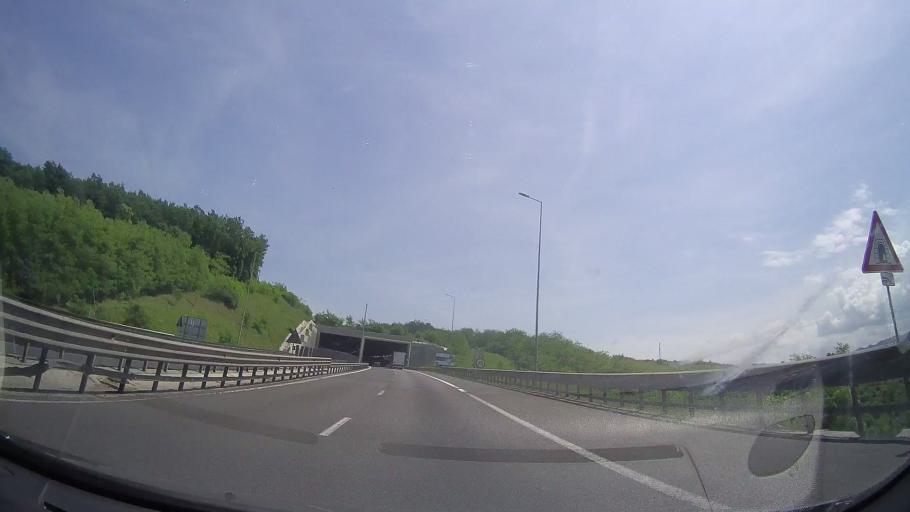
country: RO
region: Sibiu
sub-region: Comuna Orlat
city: Orlat
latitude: 45.7795
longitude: 23.9560
